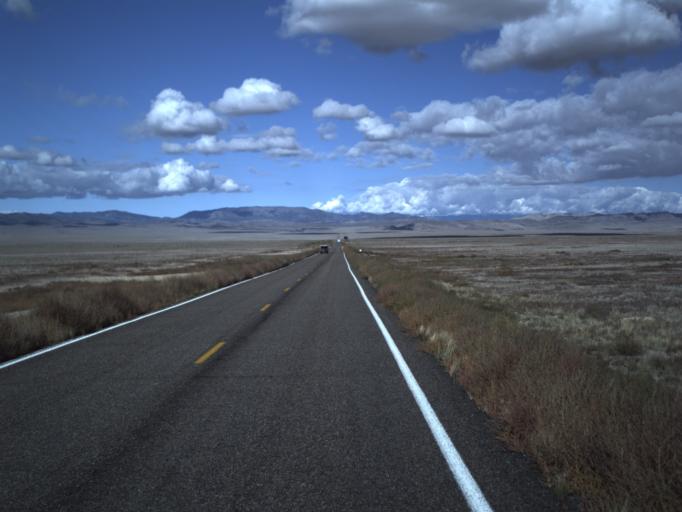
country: US
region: Utah
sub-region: Beaver County
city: Milford
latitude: 38.5198
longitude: -113.6480
